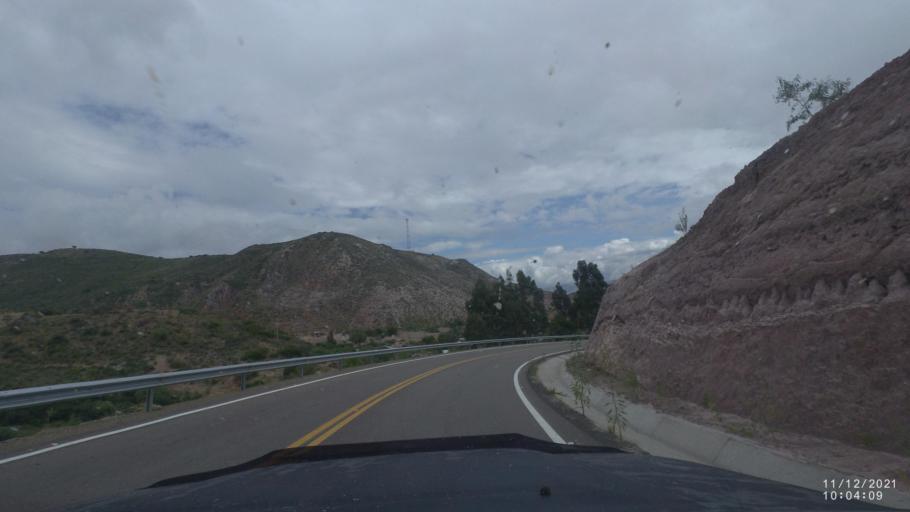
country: BO
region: Cochabamba
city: Cliza
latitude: -17.7133
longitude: -65.9423
